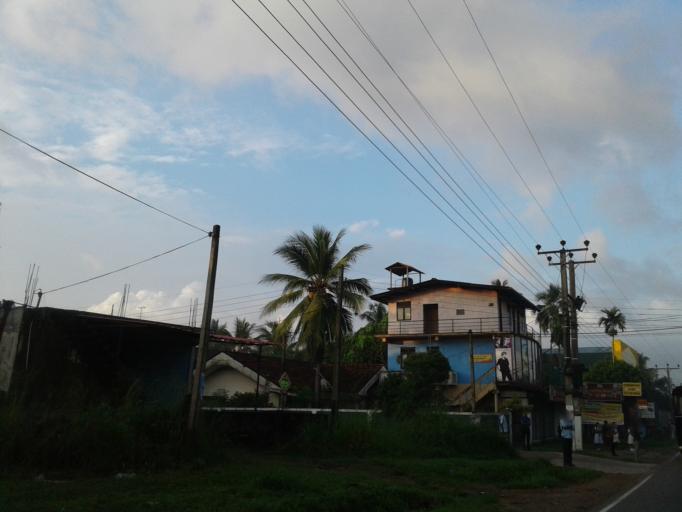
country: LK
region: Western
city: Kelaniya
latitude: 6.9756
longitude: 80.0046
